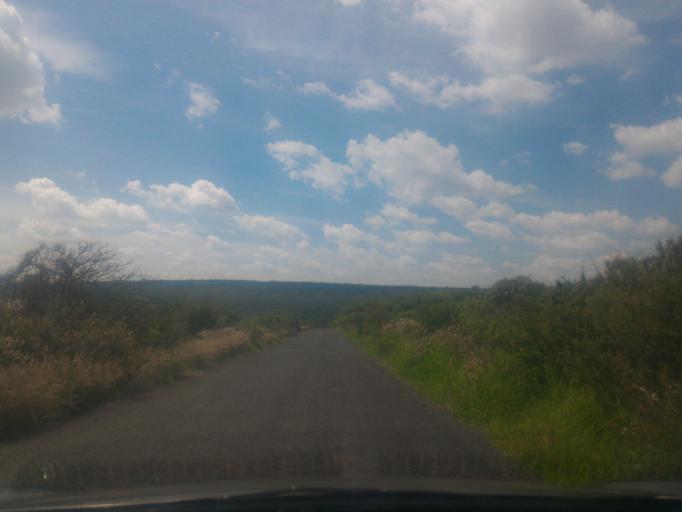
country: MX
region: Guanajuato
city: Ciudad Manuel Doblado
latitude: 20.8342
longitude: -102.0391
